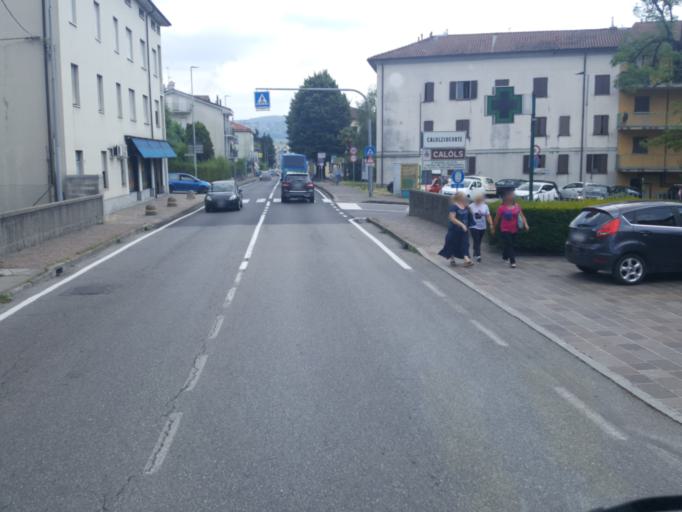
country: IT
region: Lombardy
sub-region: Provincia di Lecco
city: Vercurago
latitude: 45.8074
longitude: 9.4242
